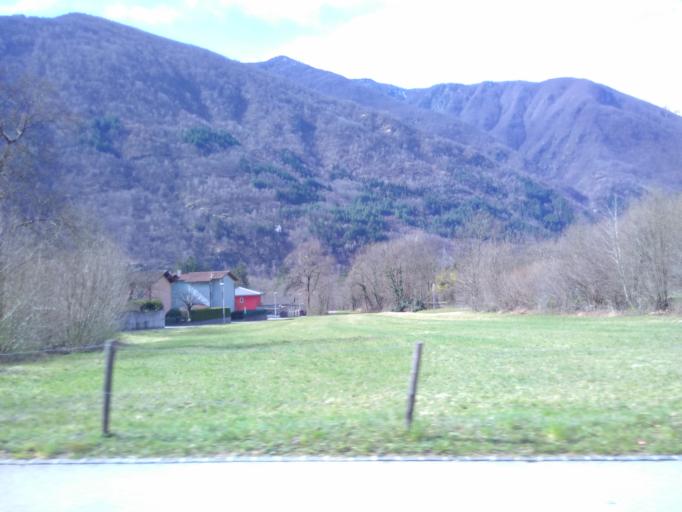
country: CH
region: Ticino
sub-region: Locarno District
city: Verscio
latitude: 46.2268
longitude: 8.7403
